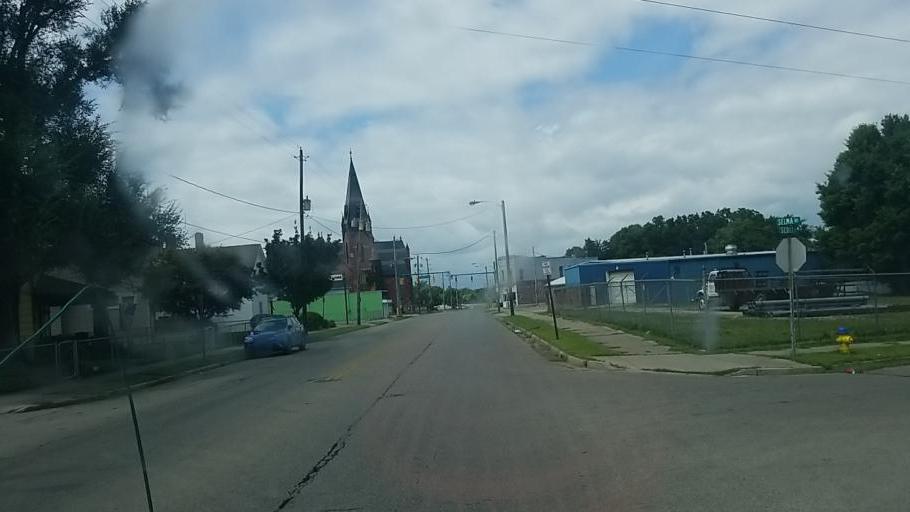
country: US
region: Ohio
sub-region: Clark County
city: Springfield
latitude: 39.9155
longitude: -83.8034
